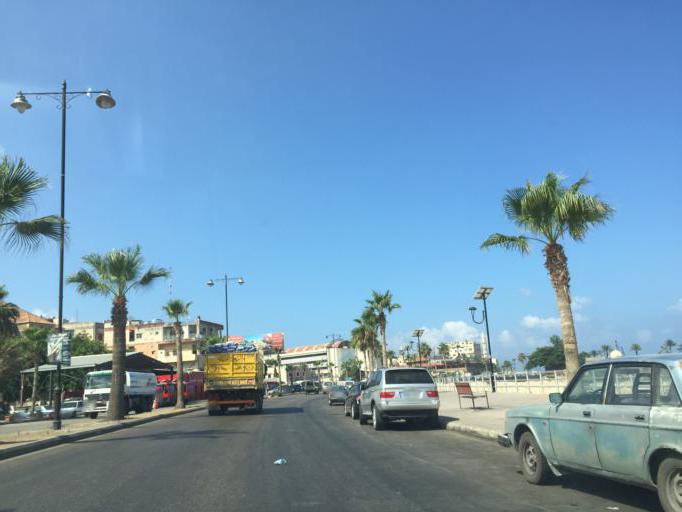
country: LB
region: Liban-Sud
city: Sidon
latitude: 33.5673
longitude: 35.3755
